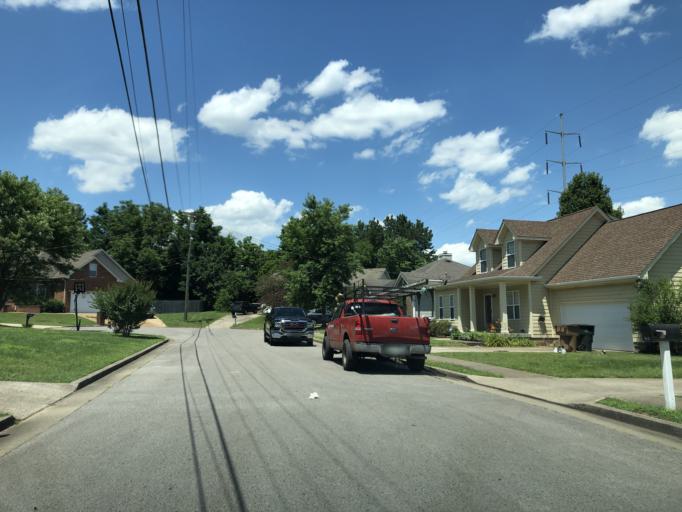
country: US
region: Tennessee
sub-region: Davidson County
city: Nashville
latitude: 36.1847
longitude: -86.7212
